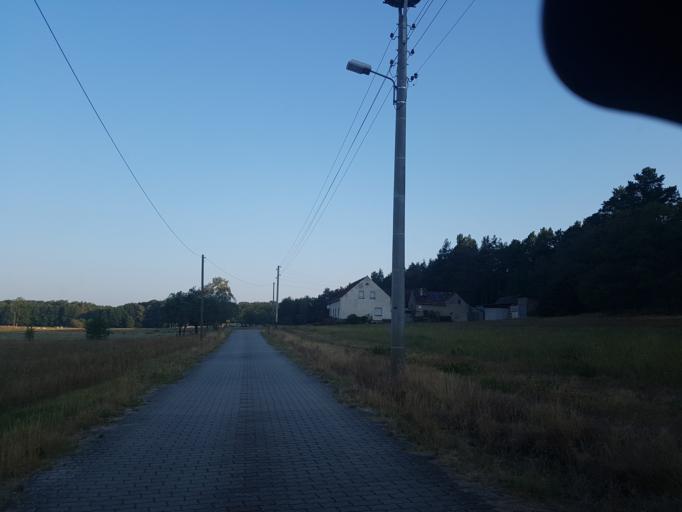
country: DE
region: Brandenburg
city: Falkenberg
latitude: 51.6458
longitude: 13.2910
